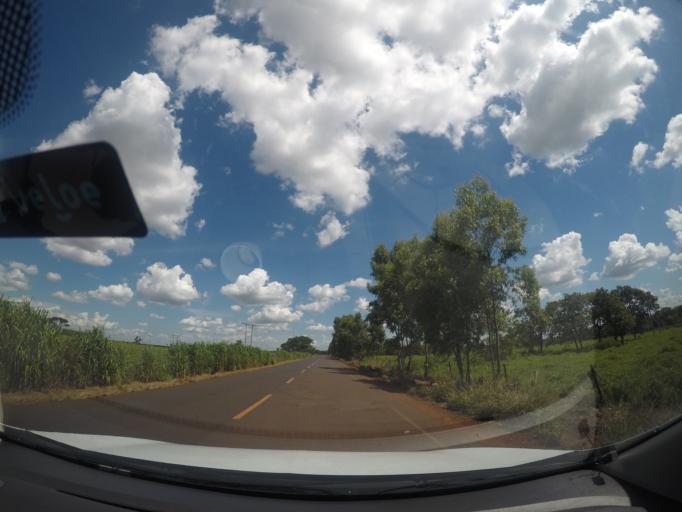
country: BR
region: Minas Gerais
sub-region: Frutal
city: Frutal
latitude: -19.8376
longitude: -48.7357
